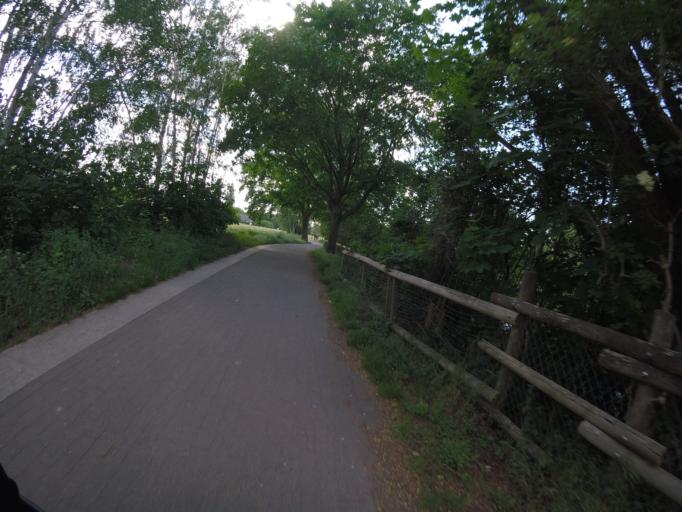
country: DE
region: Berlin
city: Staaken
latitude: 52.5289
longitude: 13.1498
